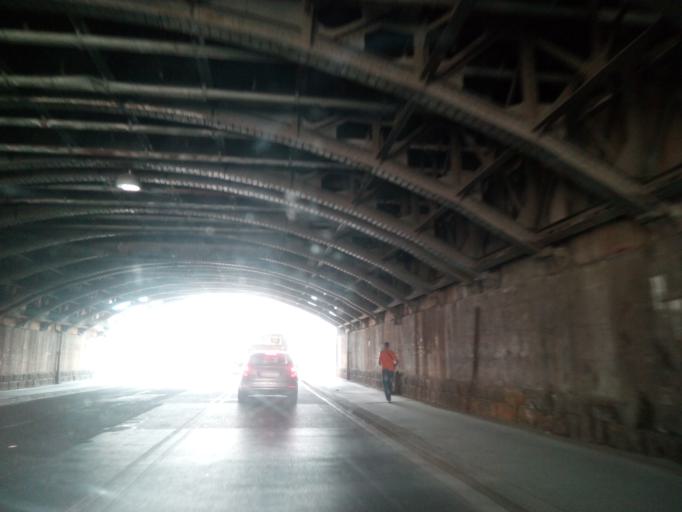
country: CZ
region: South Moravian
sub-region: Mesto Brno
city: Brno
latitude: 49.1889
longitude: 16.6095
